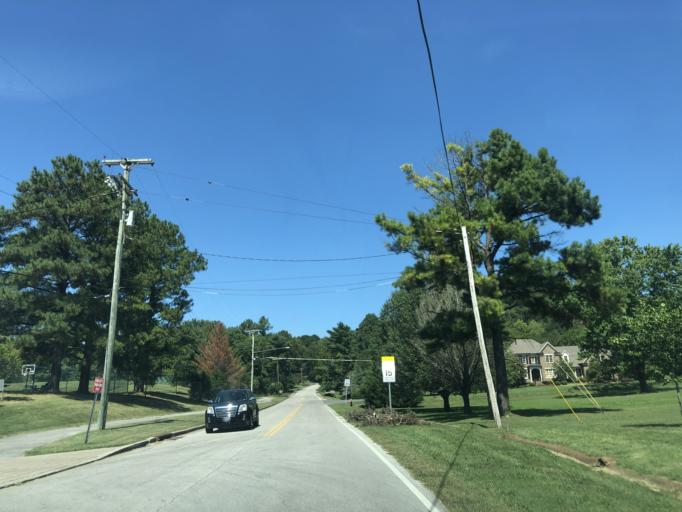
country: US
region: Tennessee
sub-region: Davidson County
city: Forest Hills
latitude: 36.0626
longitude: -86.8330
